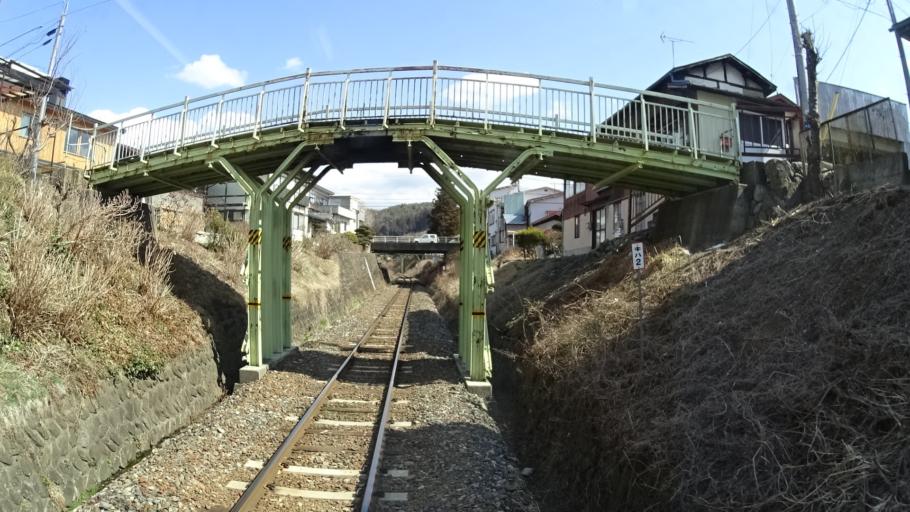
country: JP
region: Iwate
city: Tono
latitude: 39.3317
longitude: 141.5337
